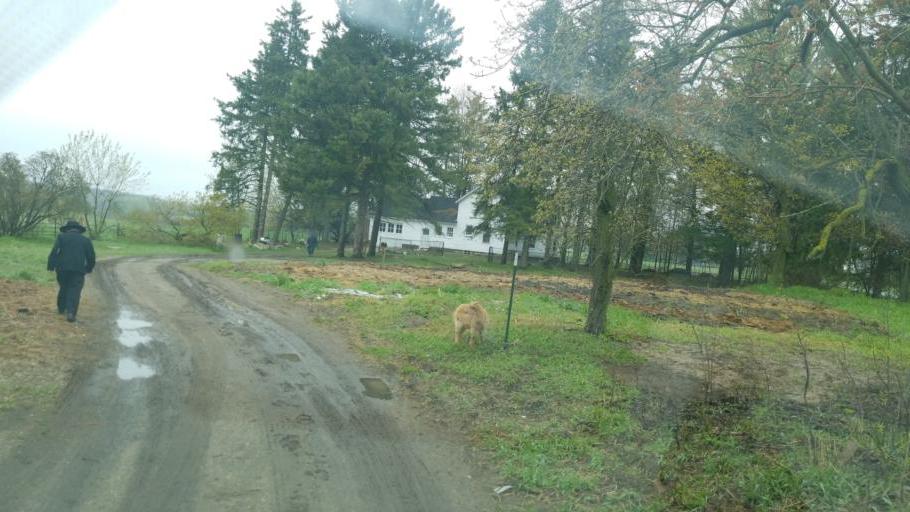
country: US
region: Michigan
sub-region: Mecosta County
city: Canadian Lakes
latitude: 43.5815
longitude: -85.3938
